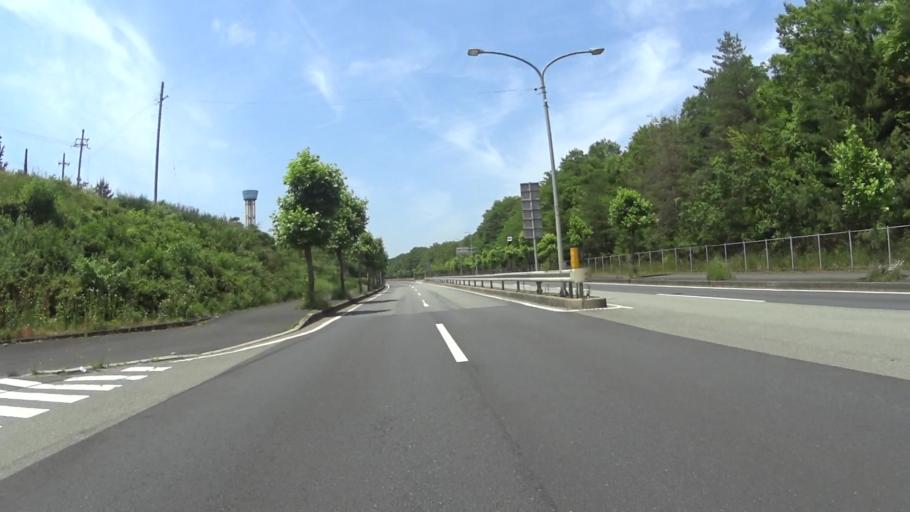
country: JP
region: Kyoto
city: Fukuchiyama
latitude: 35.2772
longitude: 135.1824
